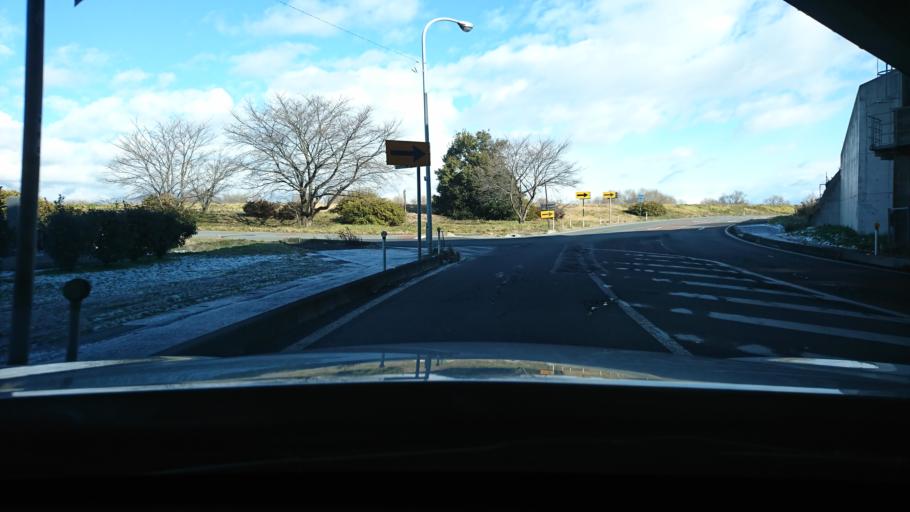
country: JP
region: Nagano
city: Nagano-shi
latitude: 36.5550
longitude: 138.1489
